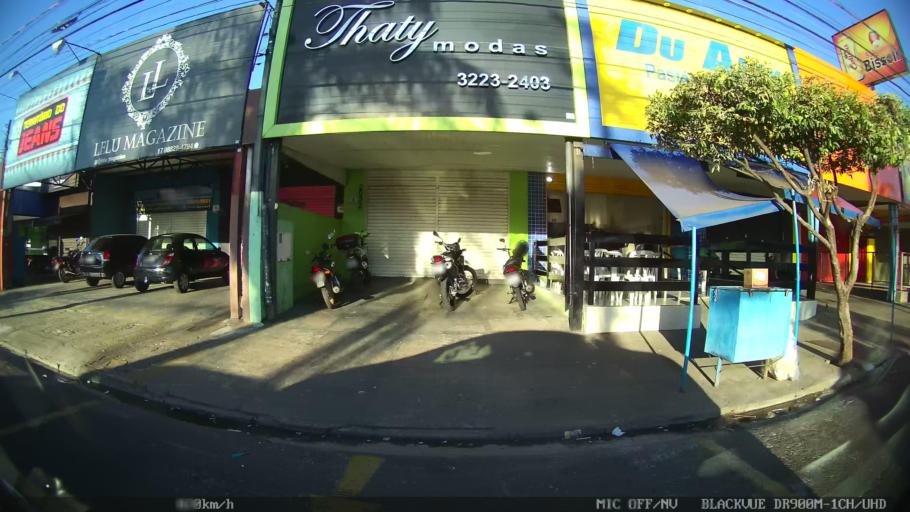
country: BR
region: Sao Paulo
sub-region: Sao Jose Do Rio Preto
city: Sao Jose do Rio Preto
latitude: -20.7801
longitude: -49.3675
